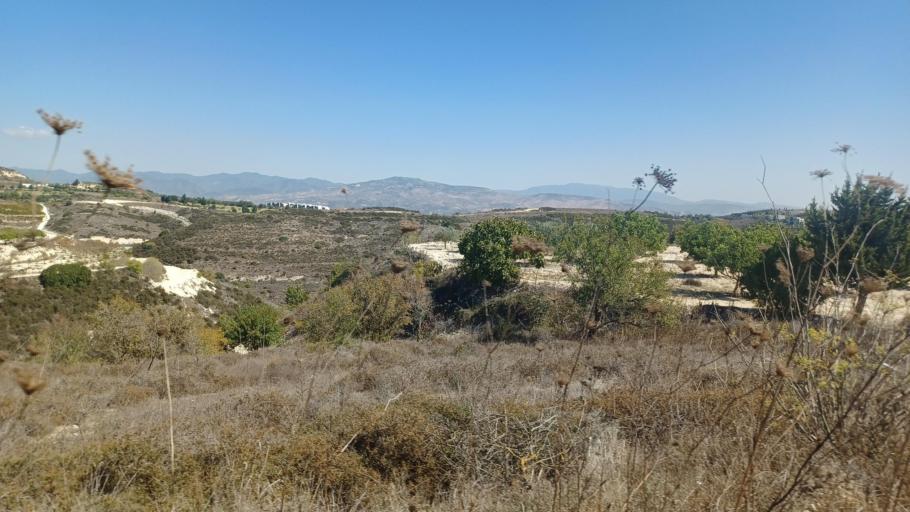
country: CY
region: Pafos
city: Mesogi
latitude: 34.8166
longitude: 32.4880
